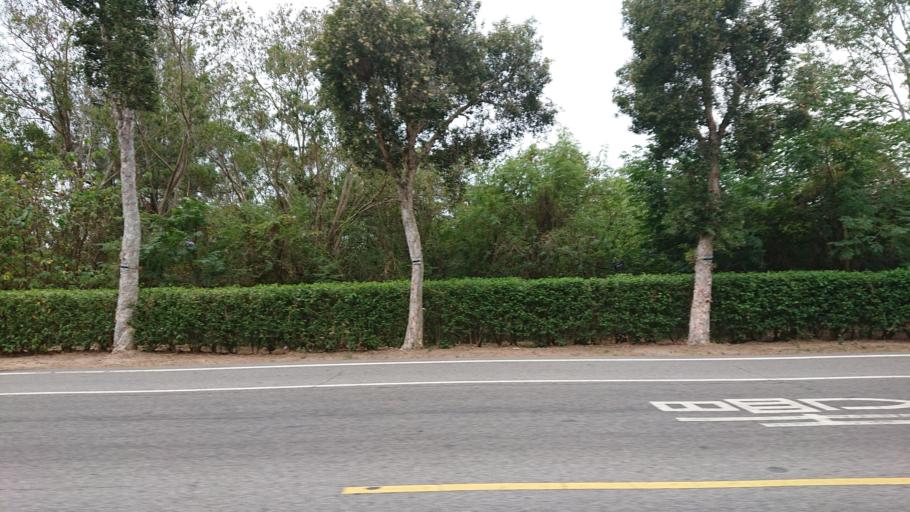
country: TW
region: Fukien
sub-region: Kinmen
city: Jincheng
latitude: 24.4383
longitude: 118.4005
